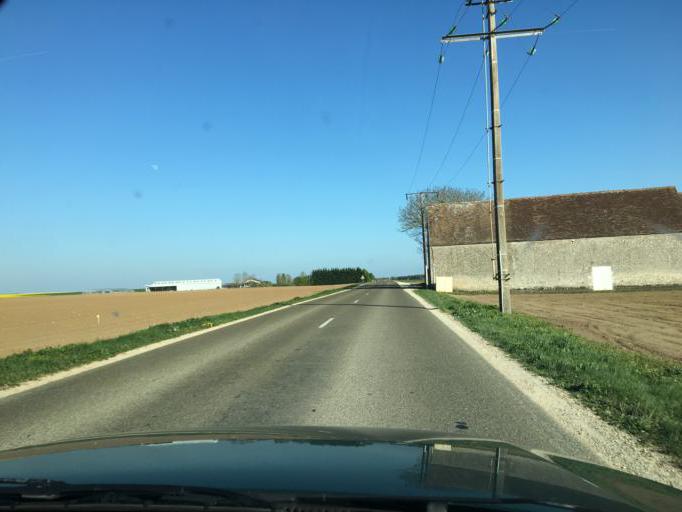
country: FR
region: Centre
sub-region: Departement du Loiret
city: Baule
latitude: 47.8540
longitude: 1.6154
